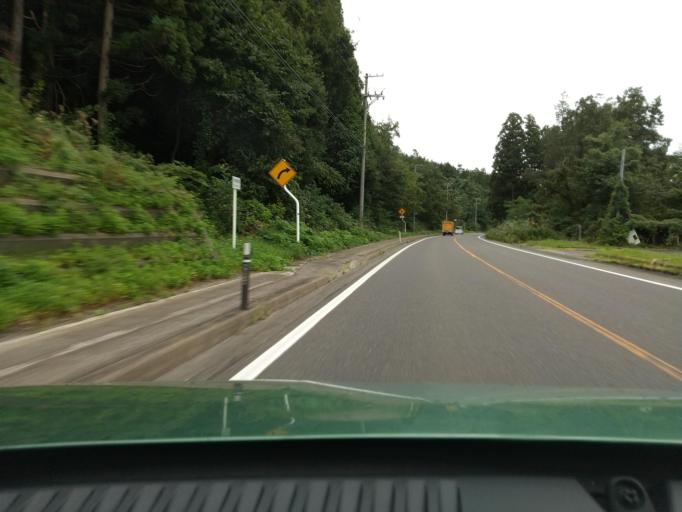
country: JP
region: Akita
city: Yokotemachi
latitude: 39.3389
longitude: 140.5603
